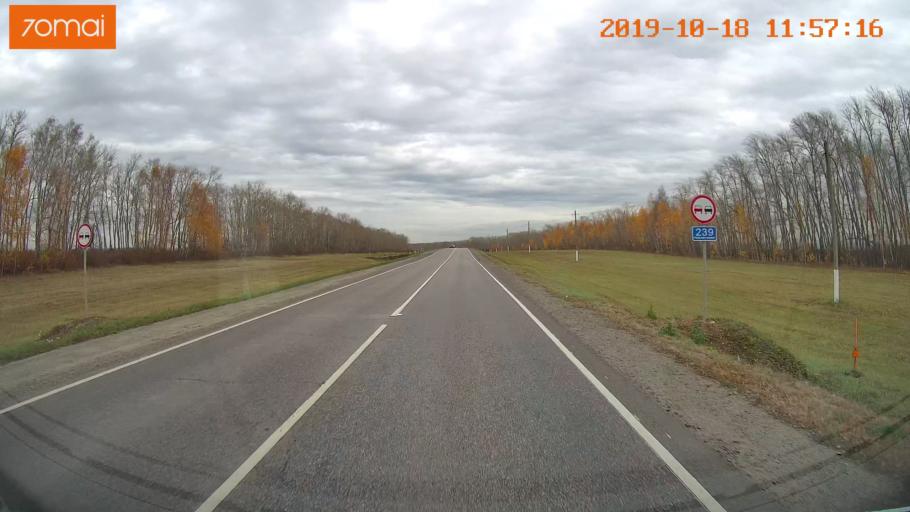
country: RU
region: Rjazan
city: Mikhaylov
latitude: 54.2663
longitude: 39.1390
